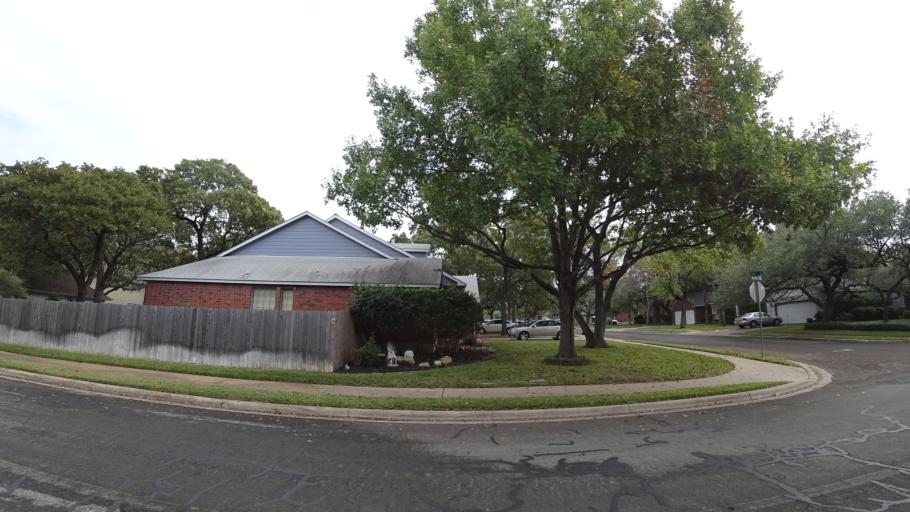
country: US
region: Texas
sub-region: Williamson County
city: Brushy Creek
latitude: 30.5171
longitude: -97.7158
